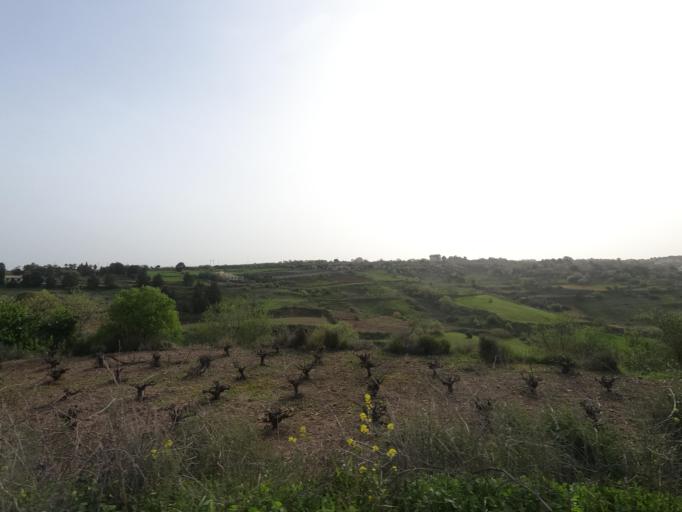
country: CY
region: Pafos
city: Pegeia
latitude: 34.9607
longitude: 32.3804
